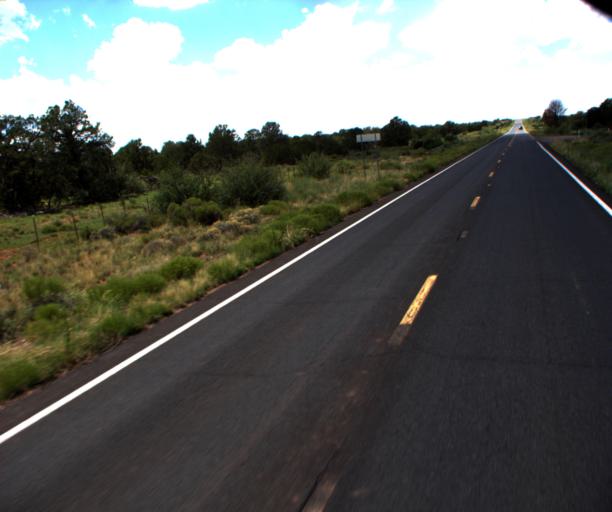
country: US
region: Arizona
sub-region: Coconino County
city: Parks
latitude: 35.6091
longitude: -112.0581
